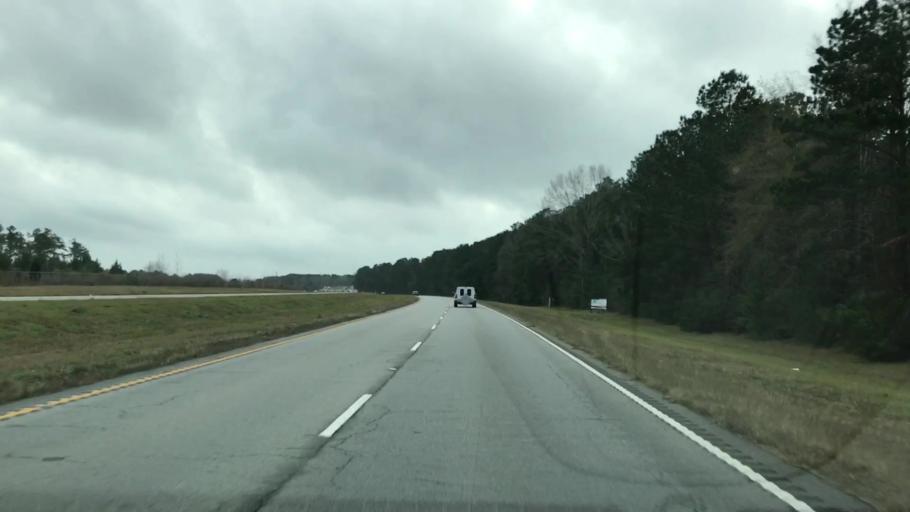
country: US
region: South Carolina
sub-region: Berkeley County
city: Moncks Corner
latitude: 33.1606
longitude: -80.0318
